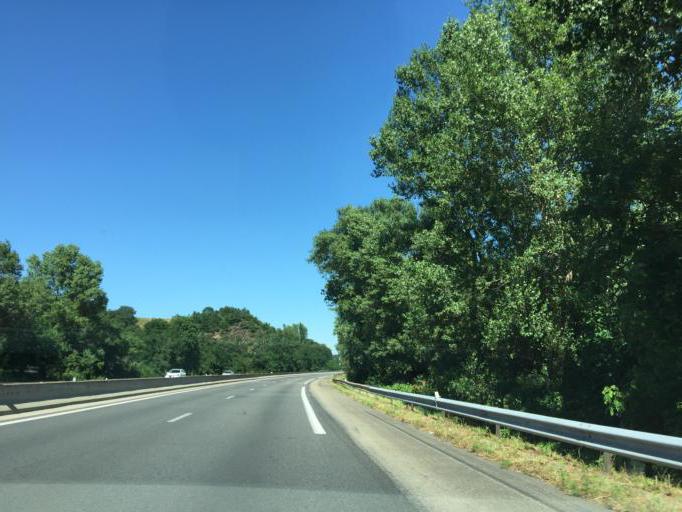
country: FR
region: Rhone-Alpes
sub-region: Departement du Rhone
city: Echalas
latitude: 45.5617
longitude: 4.6968
